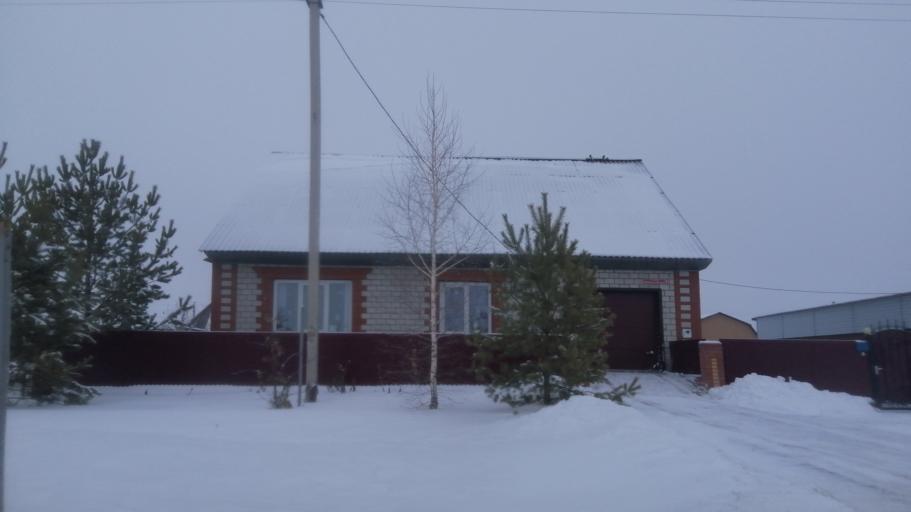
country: RU
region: Novosibirsk
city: Krasnozerskoye
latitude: 53.9923
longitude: 79.2610
